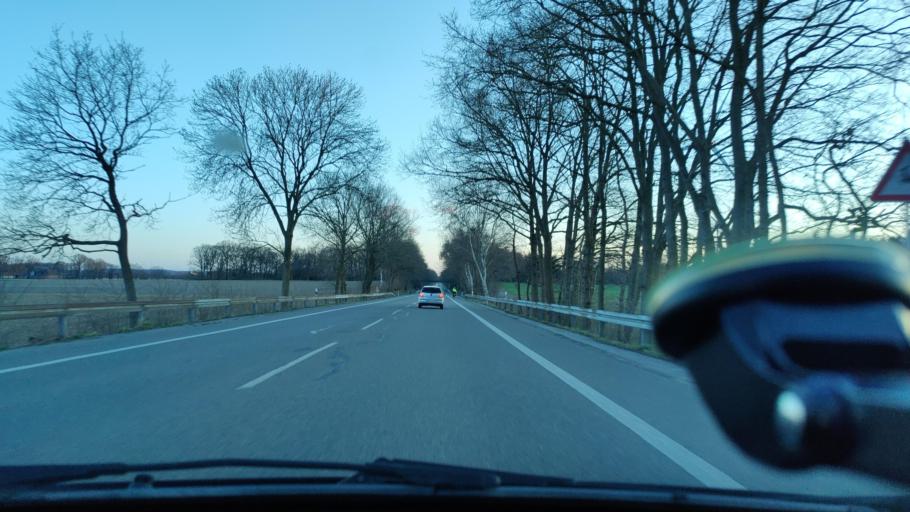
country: DE
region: North Rhine-Westphalia
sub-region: Regierungsbezirk Munster
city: Haltern
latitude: 51.7732
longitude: 7.2037
